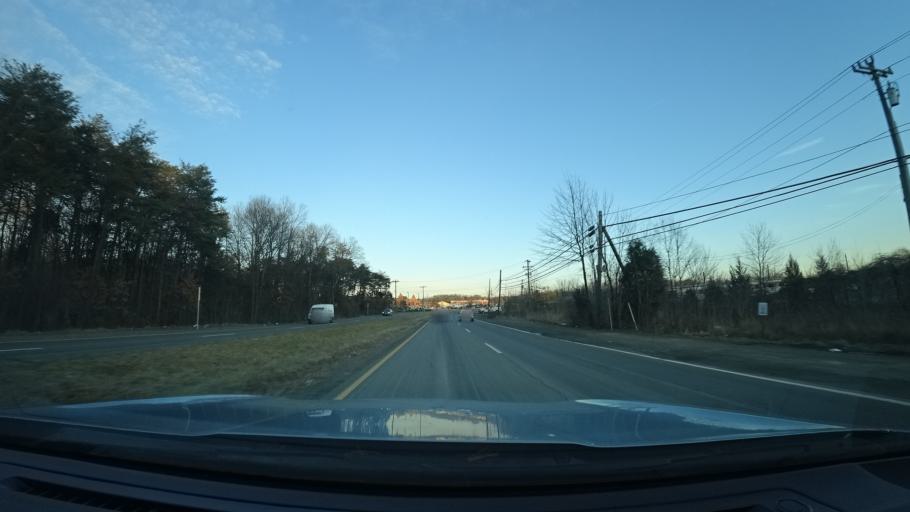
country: US
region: Virginia
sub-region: Loudoun County
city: Oak Grove
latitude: 38.9781
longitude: -77.4185
